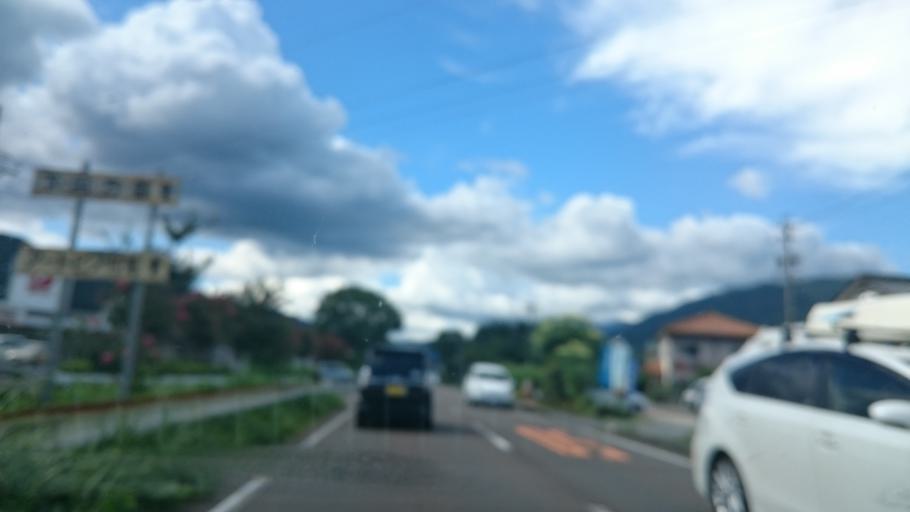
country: JP
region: Gifu
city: Nakatsugawa
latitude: 35.6404
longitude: 137.4440
